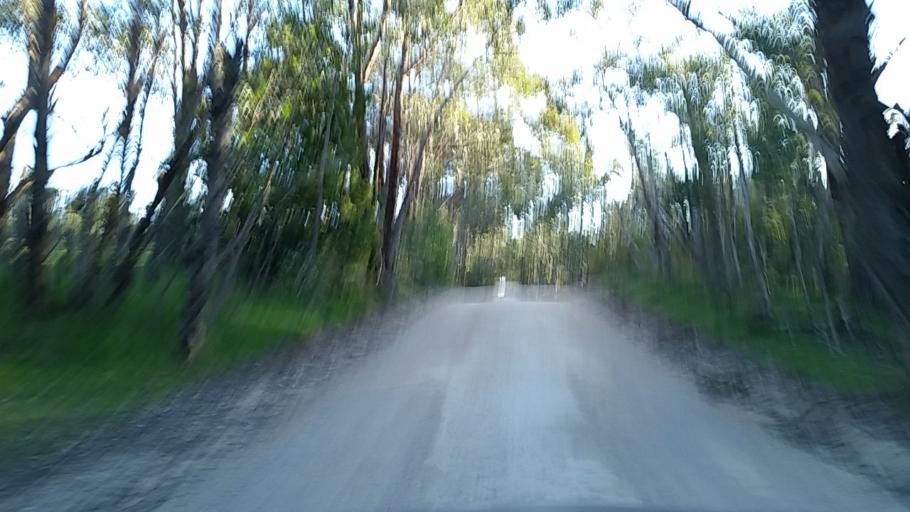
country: AU
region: South Australia
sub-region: Alexandrina
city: Mount Compass
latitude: -35.3013
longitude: 138.6799
